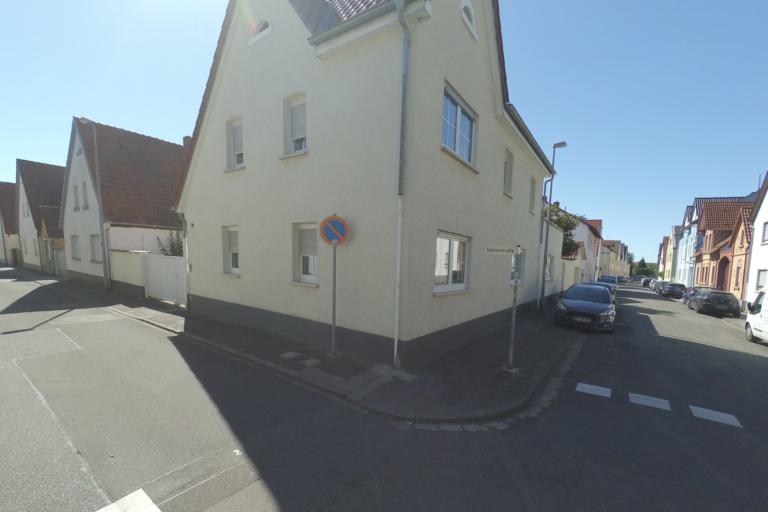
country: DE
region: Hesse
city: Viernheim
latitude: 49.5418
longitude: 8.5770
